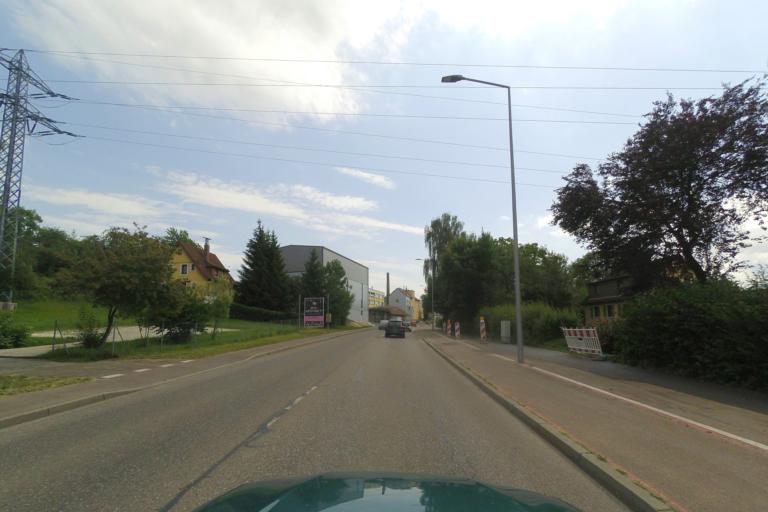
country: DE
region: Baden-Wuerttemberg
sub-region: Regierungsbezirk Stuttgart
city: Aalen
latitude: 48.8522
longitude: 10.1000
